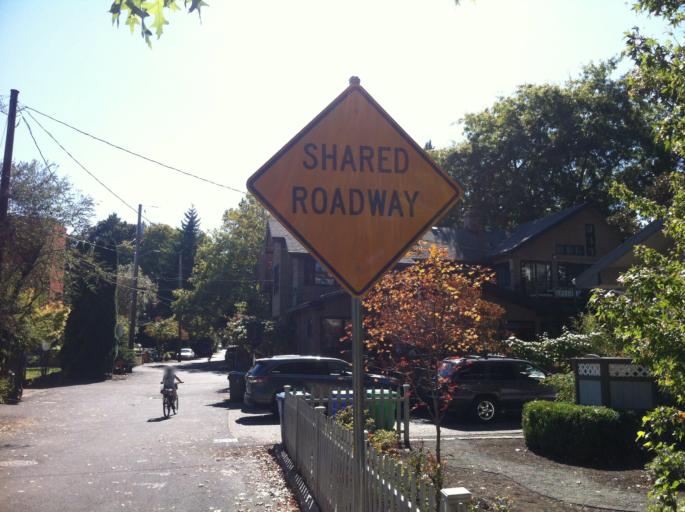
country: US
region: Oregon
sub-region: Clackamas County
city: Milwaukie
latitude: 45.4717
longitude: -122.6701
